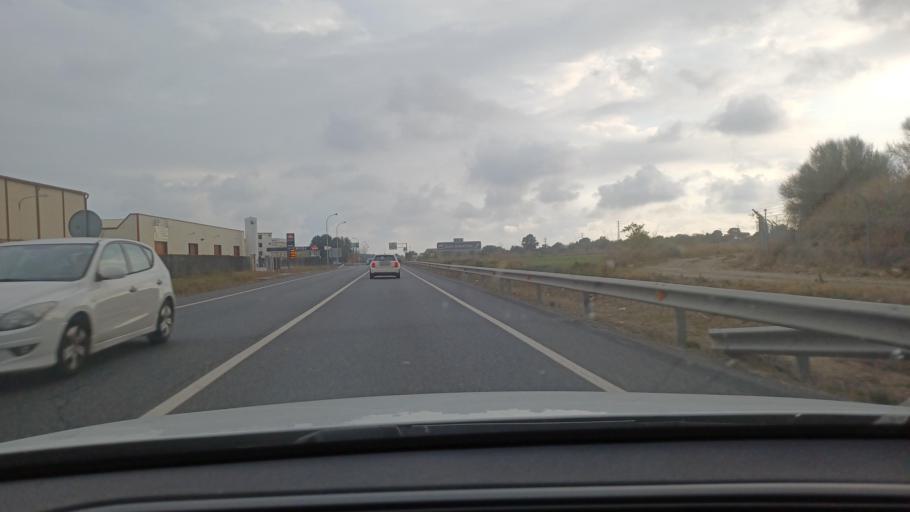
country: ES
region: Catalonia
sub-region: Provincia de Tarragona
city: la Pobla de Mafumet
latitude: 41.1910
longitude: 1.2429
